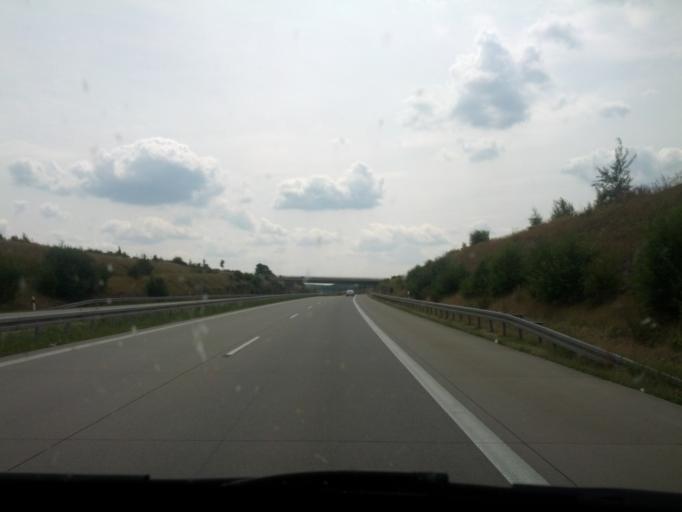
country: DE
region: Saxony
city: Liebstadt
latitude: 50.8165
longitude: 13.8855
